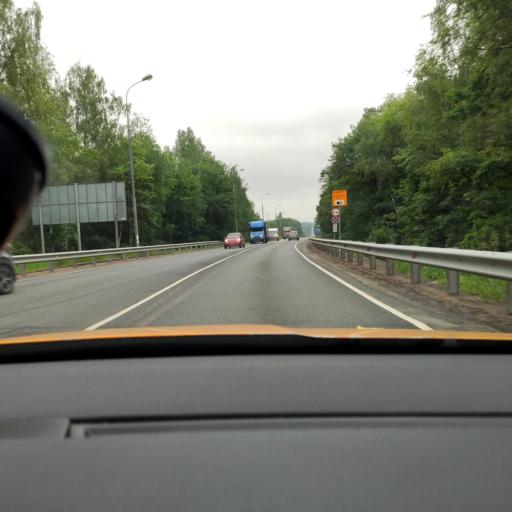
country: RU
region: Moskovskaya
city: Danki
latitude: 54.9204
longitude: 37.5096
